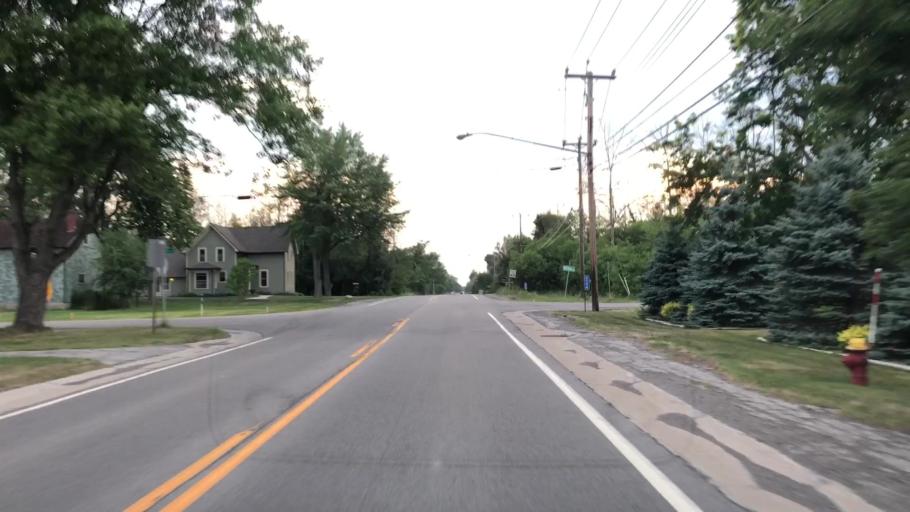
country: US
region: New York
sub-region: Erie County
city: Elma Center
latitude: 42.8392
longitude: -78.6438
